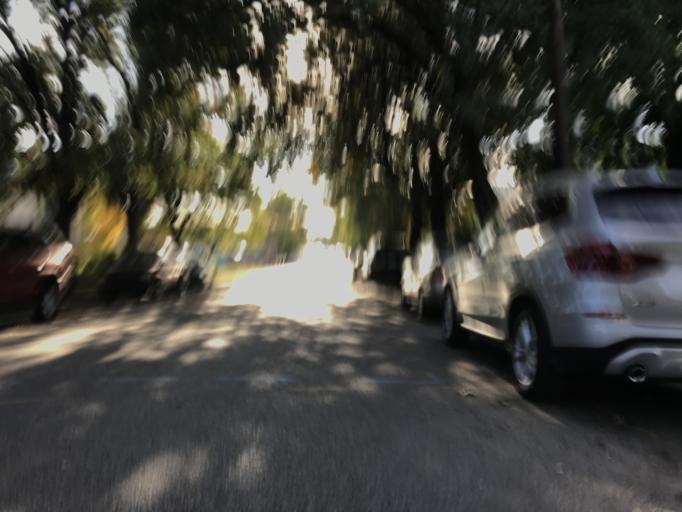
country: US
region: Indiana
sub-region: Clark County
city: Jeffersonville
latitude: 38.2572
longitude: -85.7280
